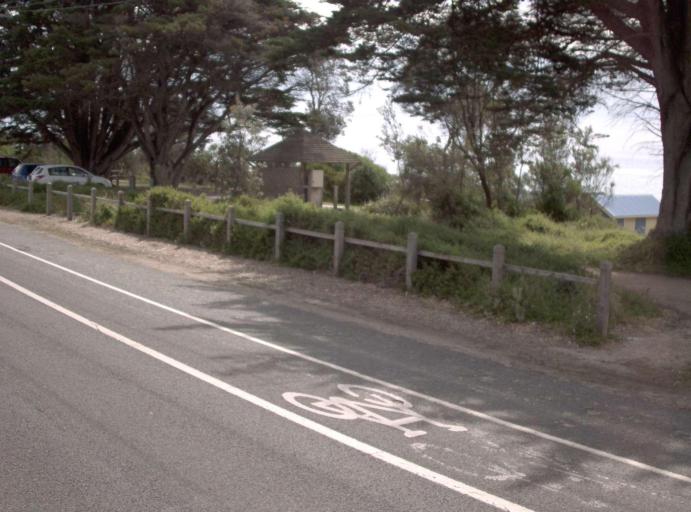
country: AU
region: Victoria
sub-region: Mornington Peninsula
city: Dromana
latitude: -38.3371
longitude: 144.9557
